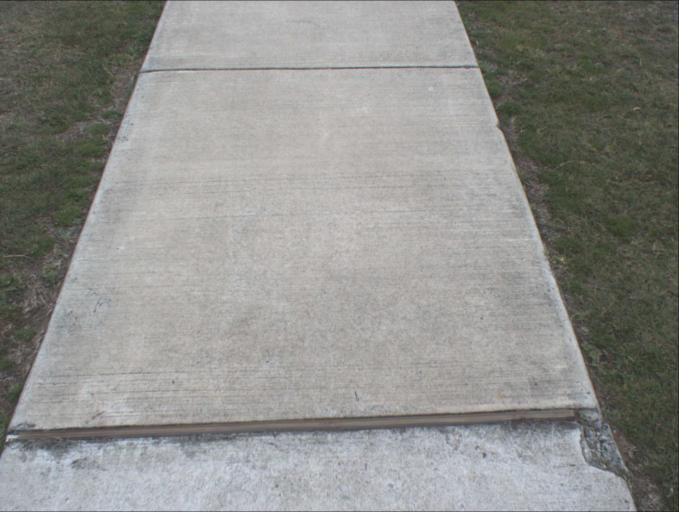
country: AU
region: Queensland
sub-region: Logan
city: Park Ridge South
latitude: -27.6780
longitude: 153.0563
